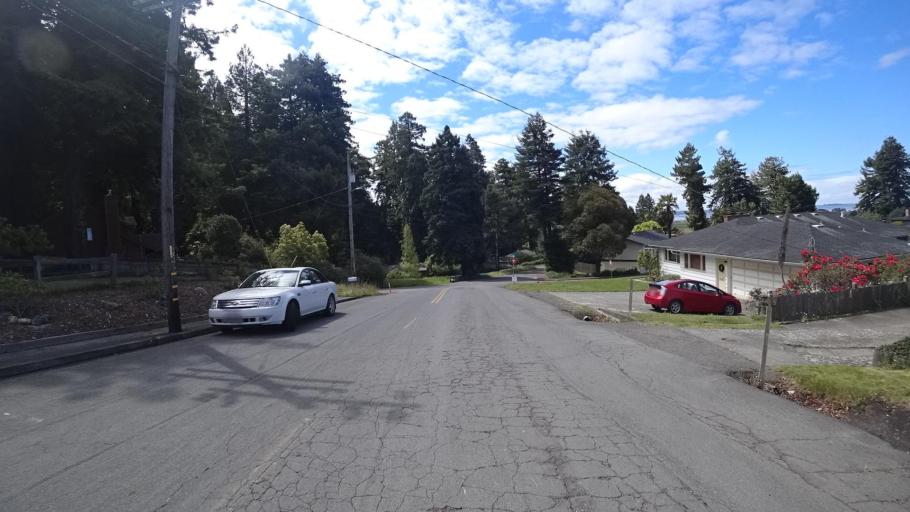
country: US
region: California
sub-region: Humboldt County
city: Arcata
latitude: 40.8669
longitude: -124.0759
